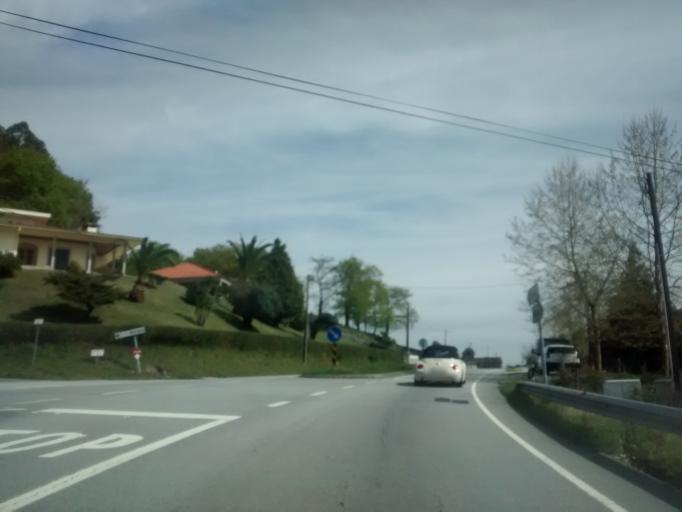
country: PT
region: Braga
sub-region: Vieira do Minho
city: Real
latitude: 41.6218
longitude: -8.2272
